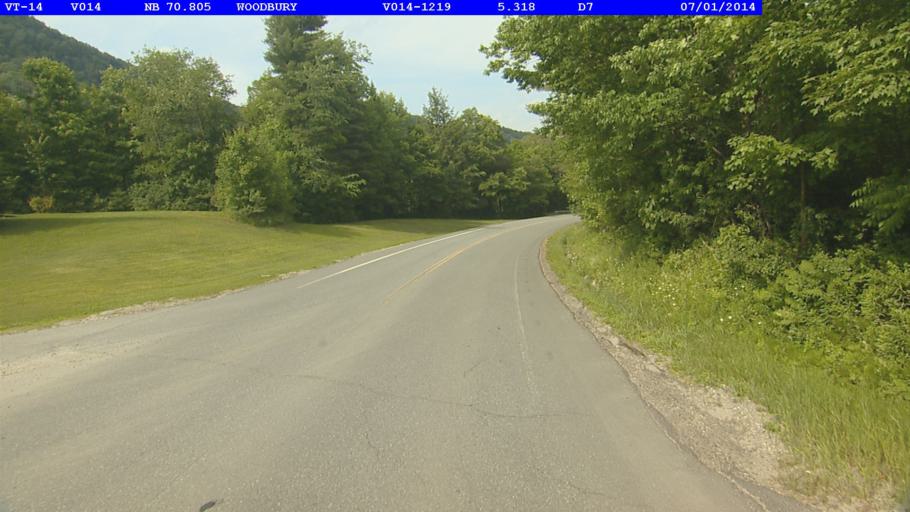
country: US
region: Vermont
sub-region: Caledonia County
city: Hardwick
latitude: 44.4634
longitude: -72.4158
